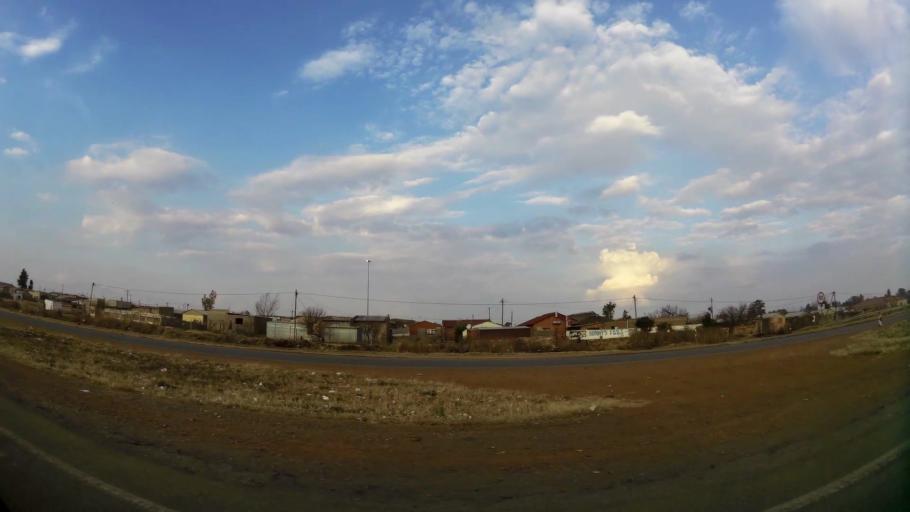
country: ZA
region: Gauteng
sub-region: Sedibeng District Municipality
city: Vanderbijlpark
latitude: -26.6031
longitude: 27.8177
